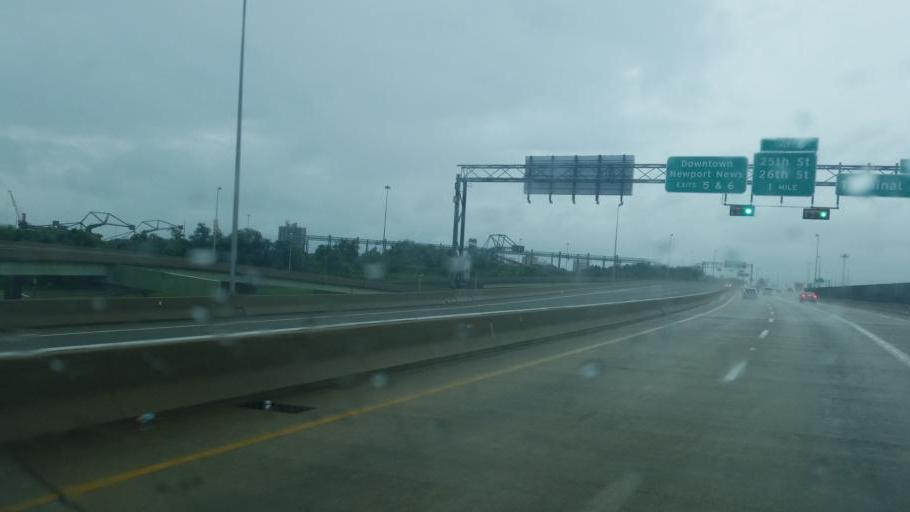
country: US
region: Virginia
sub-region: City of Newport News
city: Newport News
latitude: 36.9668
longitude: -76.4144
